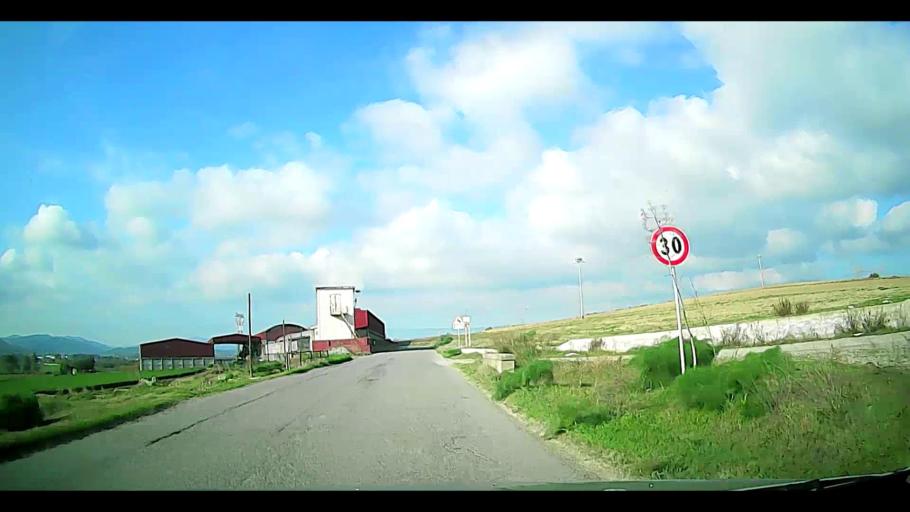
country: IT
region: Calabria
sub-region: Provincia di Crotone
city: Rocca di Neto
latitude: 39.1820
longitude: 17.0425
